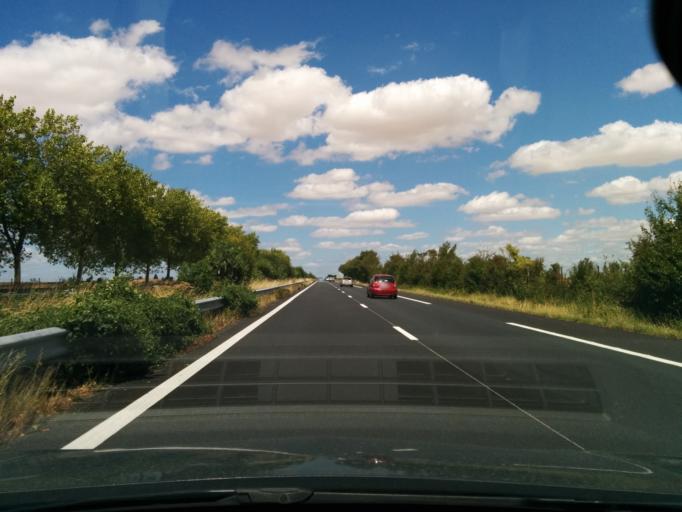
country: FR
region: Centre
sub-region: Departement de l'Indre
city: Montierchaume
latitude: 46.9391
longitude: 1.7501
